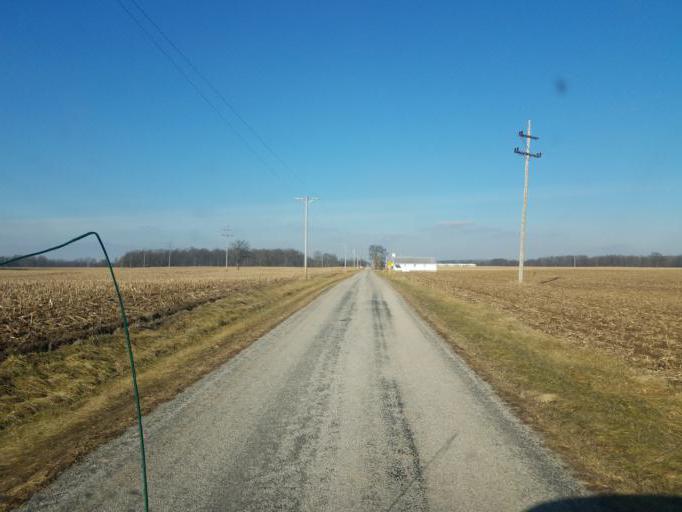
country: US
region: Ohio
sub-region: Wyandot County
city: Upper Sandusky
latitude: 40.6730
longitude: -83.3623
